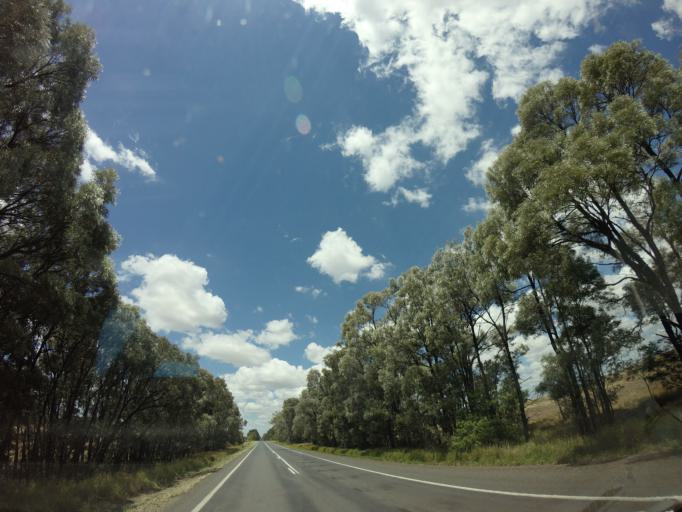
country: AU
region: Queensland
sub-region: Toowoomba
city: Oakey
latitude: -27.8953
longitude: 151.2071
